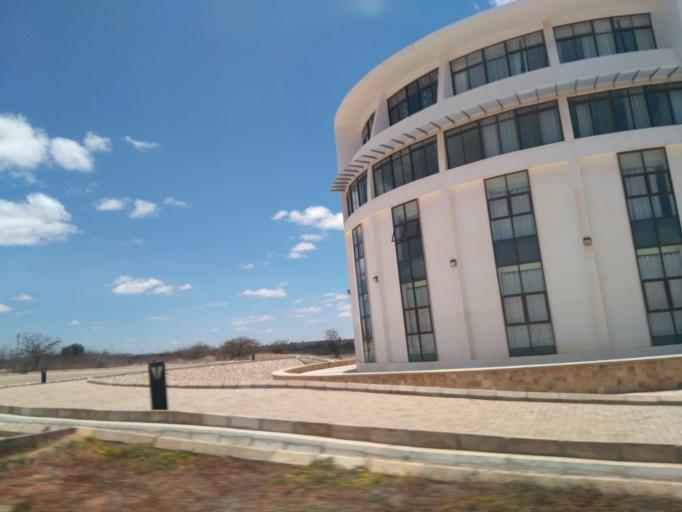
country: TZ
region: Dodoma
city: Kisasa
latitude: -6.2164
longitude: 35.8085
